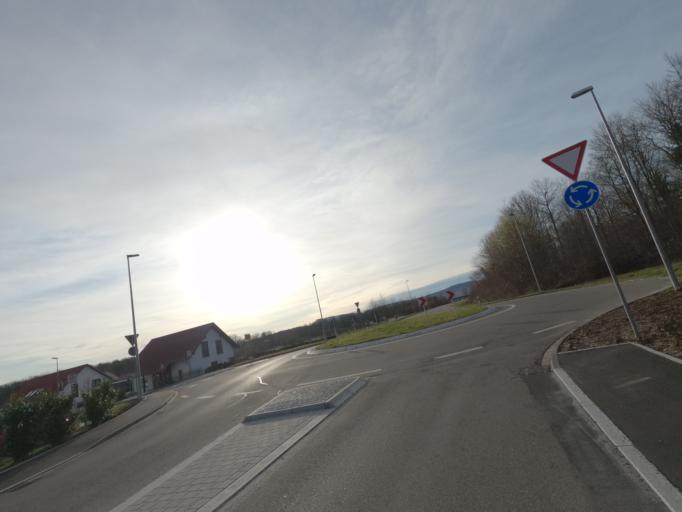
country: DE
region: Baden-Wuerttemberg
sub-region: Regierungsbezirk Stuttgart
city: Uhingen
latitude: 48.6957
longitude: 9.5820
